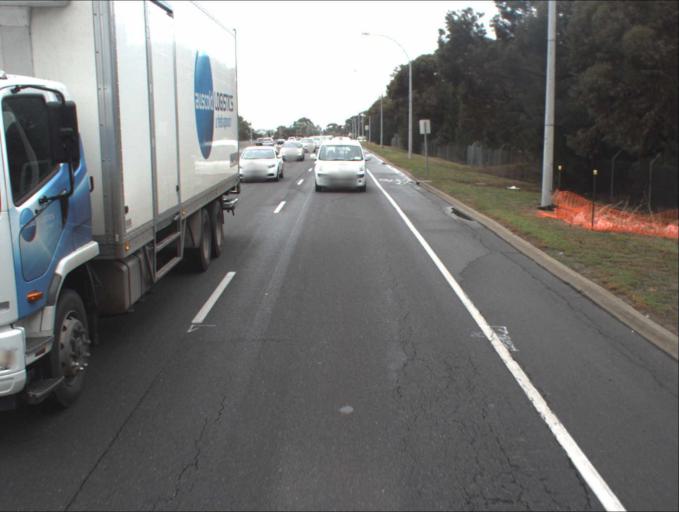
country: AU
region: South Australia
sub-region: Port Adelaide Enfield
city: Gilles Plains
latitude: -34.8494
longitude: 138.6498
